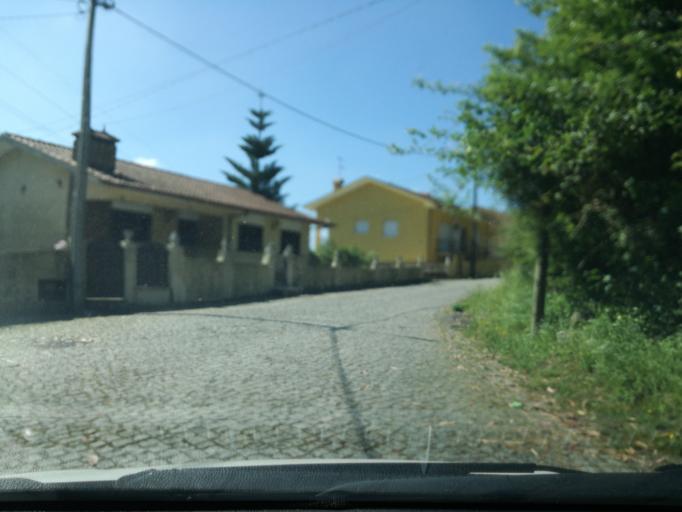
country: PT
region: Porto
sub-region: Maia
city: Nogueira
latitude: 41.2472
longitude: -8.6020
